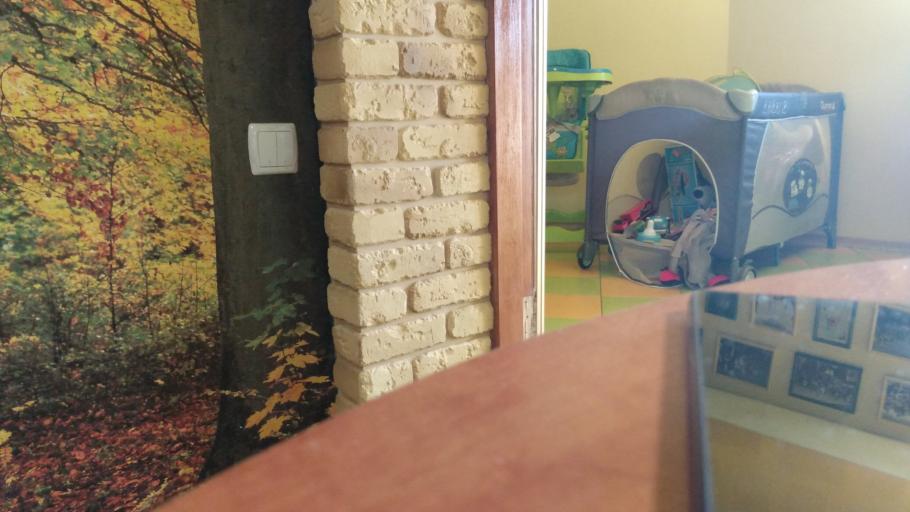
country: RU
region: Tverskaya
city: Bologoye
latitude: 57.8790
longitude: 34.2937
